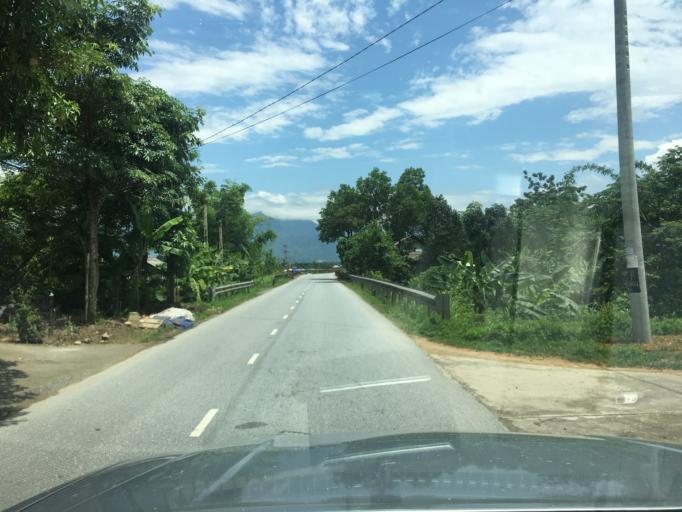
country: VN
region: Yen Bai
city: Son Thinh
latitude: 21.6235
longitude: 104.5093
